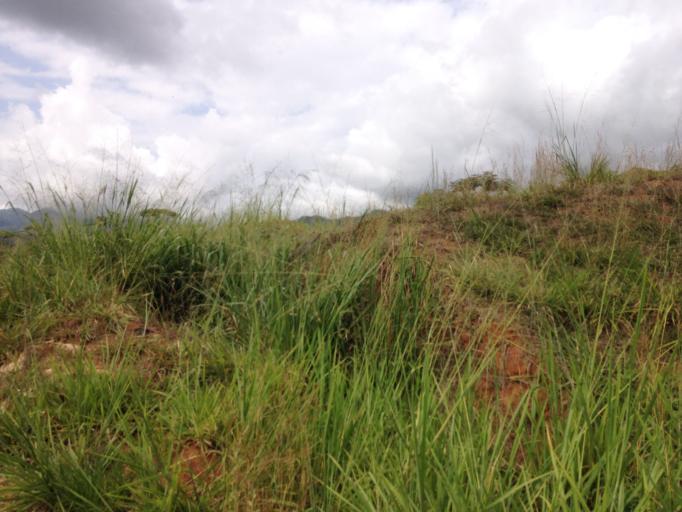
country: CO
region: Valle del Cauca
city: Cali
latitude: 3.3720
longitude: -76.5577
